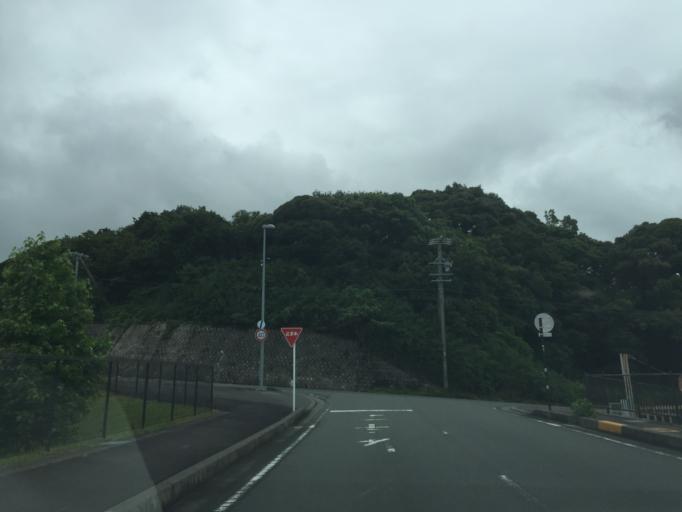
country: JP
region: Shizuoka
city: Fukuroi
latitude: 34.7690
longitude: 137.9245
